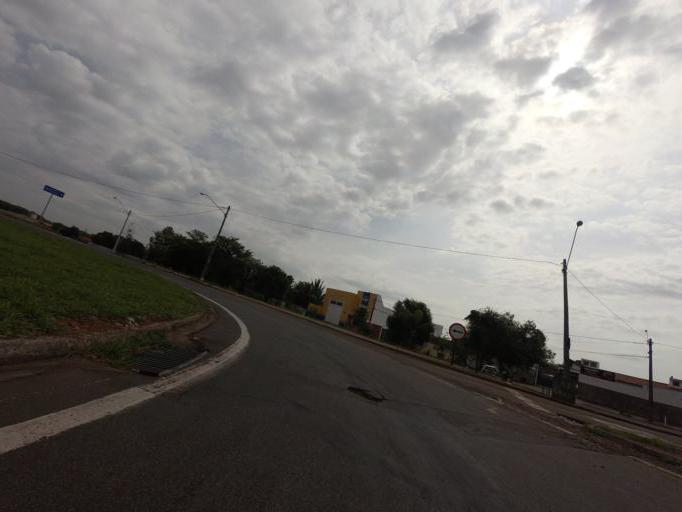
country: BR
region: Sao Paulo
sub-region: Piracicaba
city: Piracicaba
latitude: -22.7655
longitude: -47.5941
